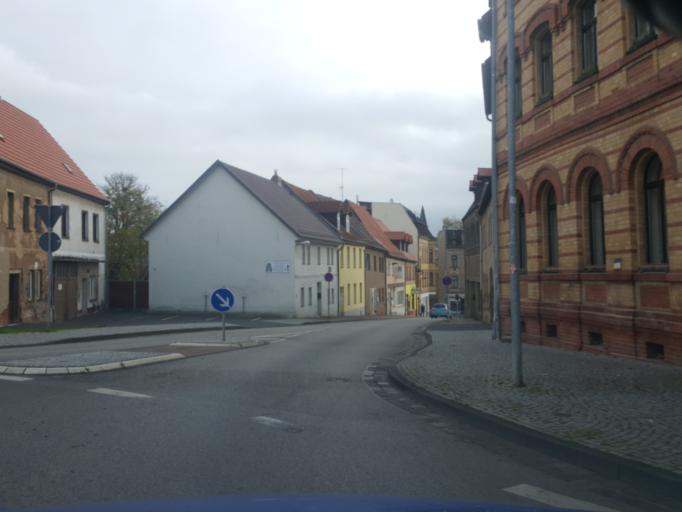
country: DE
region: Saxony-Anhalt
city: Wimmelburg
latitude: 51.5299
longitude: 11.5424
